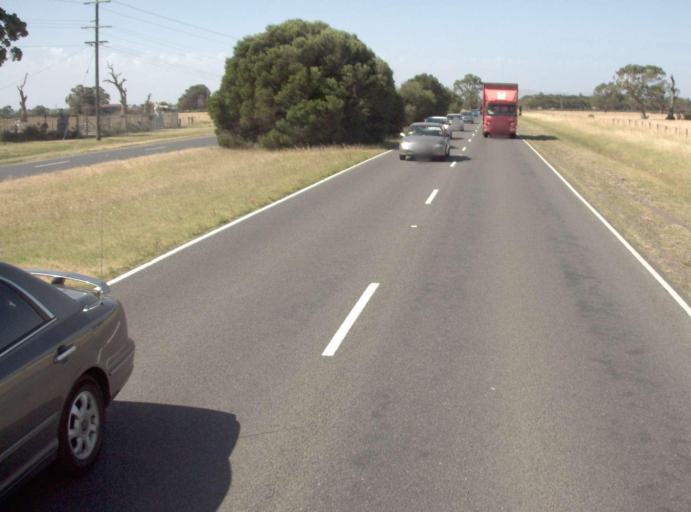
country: AU
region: Victoria
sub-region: Frankston
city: Sandhurst
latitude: -38.0638
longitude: 145.2017
